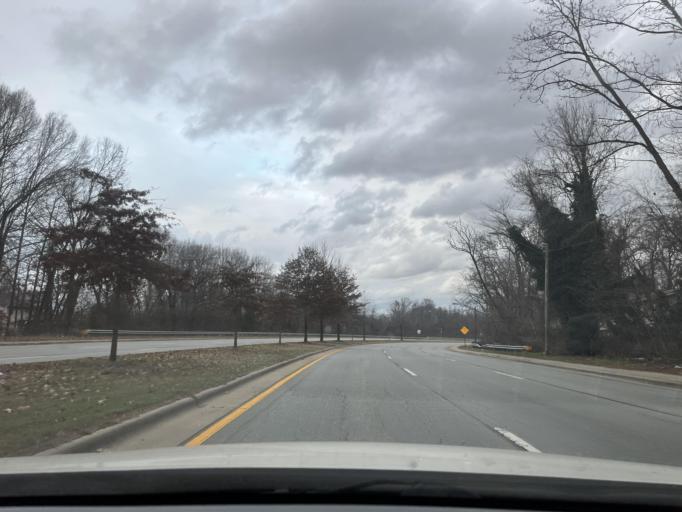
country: US
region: North Carolina
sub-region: Guilford County
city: Greensboro
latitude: 36.0444
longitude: -79.8503
